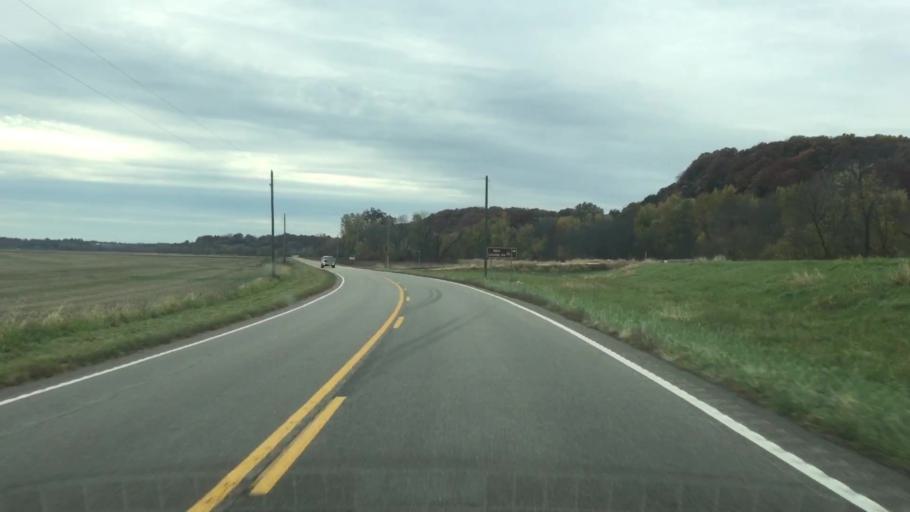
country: US
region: Missouri
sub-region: Callaway County
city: Fulton
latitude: 38.7075
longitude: -91.7832
